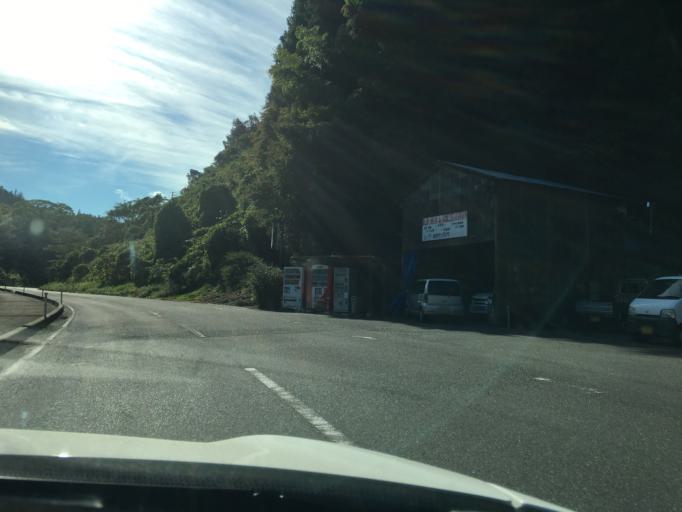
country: JP
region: Fukushima
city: Ishikawa
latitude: 37.1270
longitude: 140.5785
